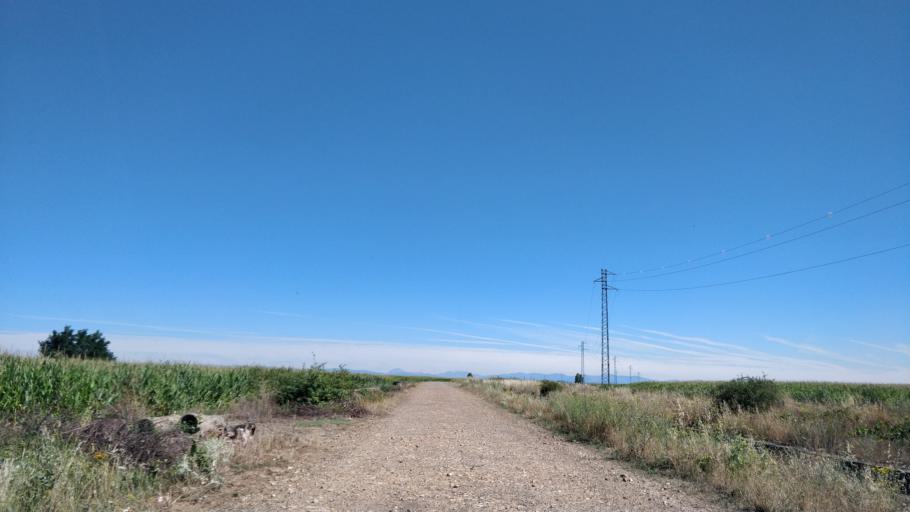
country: ES
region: Castille and Leon
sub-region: Provincia de Leon
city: Bustillo del Paramo
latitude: 42.4303
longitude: -5.8220
